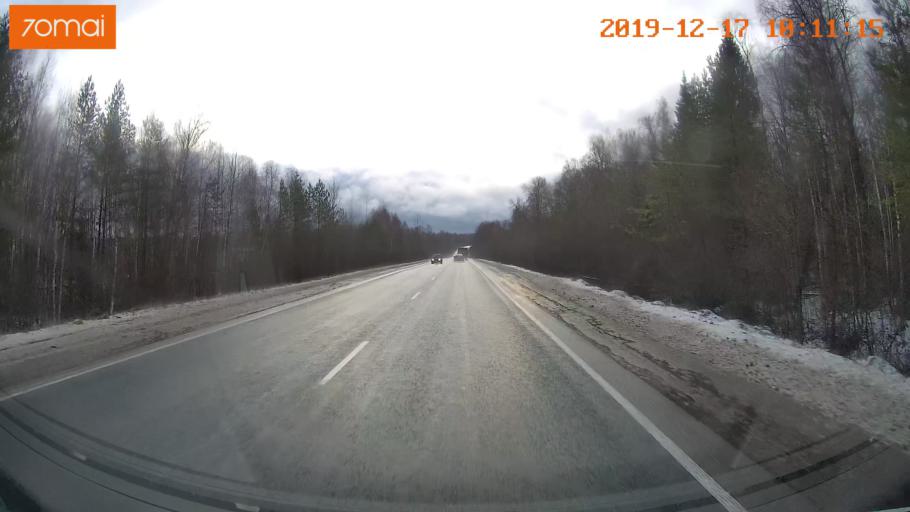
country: RU
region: Vladimir
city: Anopino
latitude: 55.8265
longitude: 40.6532
